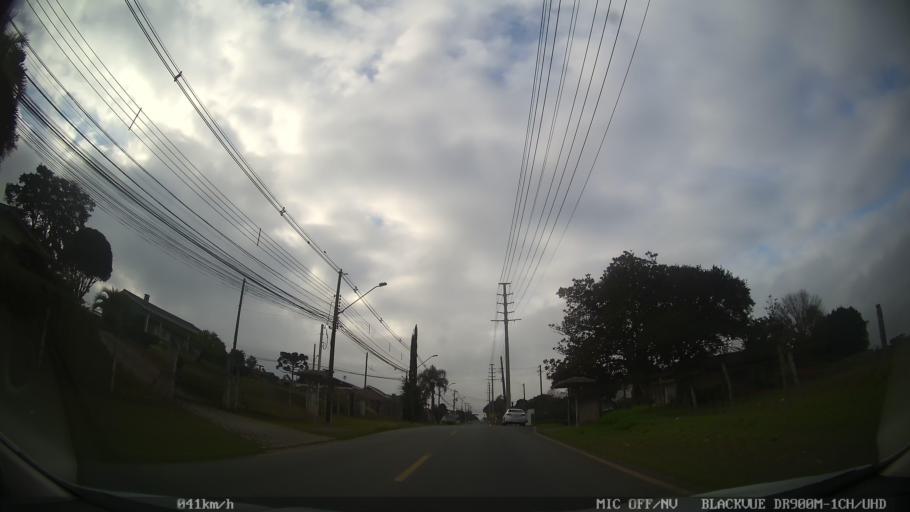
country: BR
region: Parana
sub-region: Curitiba
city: Curitiba
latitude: -25.3930
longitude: -49.3296
